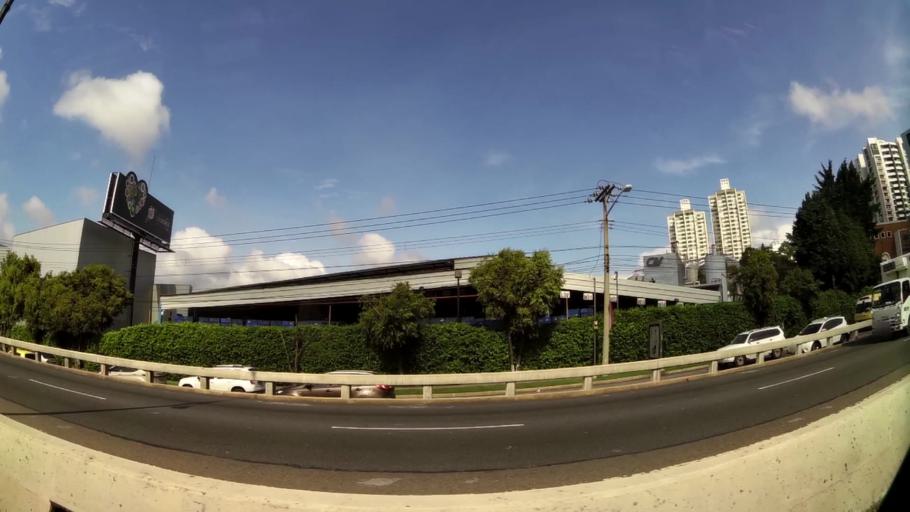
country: PA
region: Panama
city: Panama
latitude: 8.9902
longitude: -79.5318
